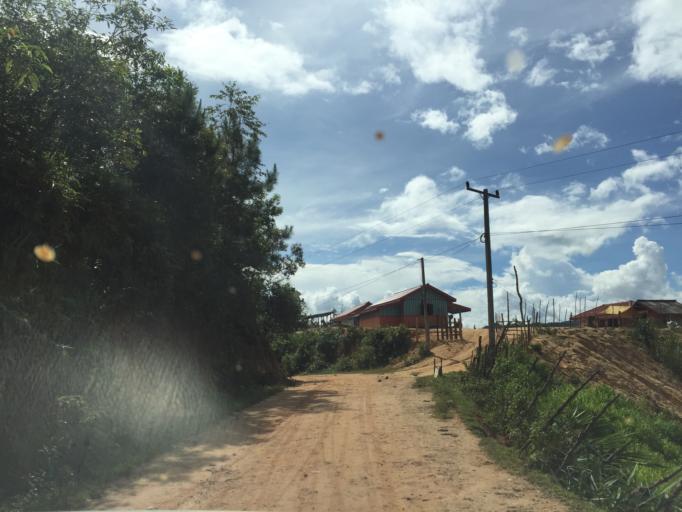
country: LA
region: Xiangkhoang
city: Muang Phonsavan
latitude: 19.3327
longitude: 103.4783
